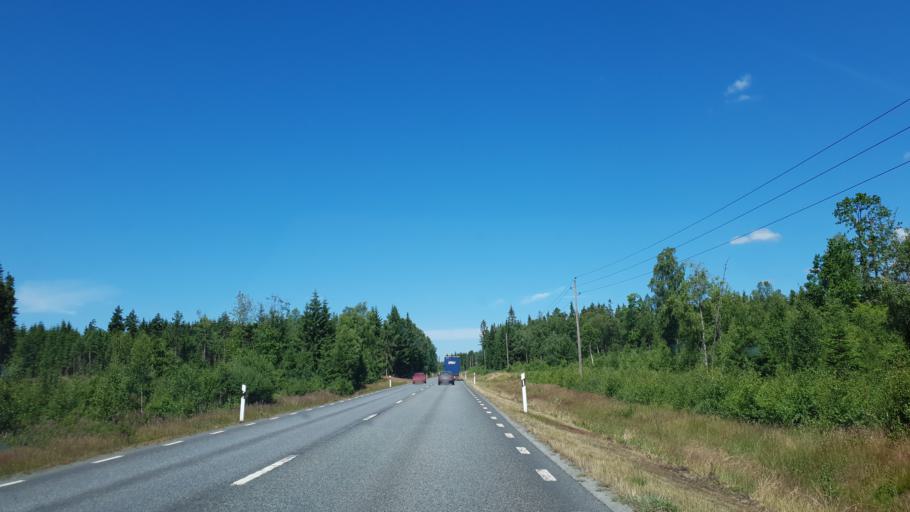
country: SE
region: Joenkoeping
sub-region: Varnamo Kommun
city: Rydaholm
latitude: 57.0369
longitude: 14.2445
